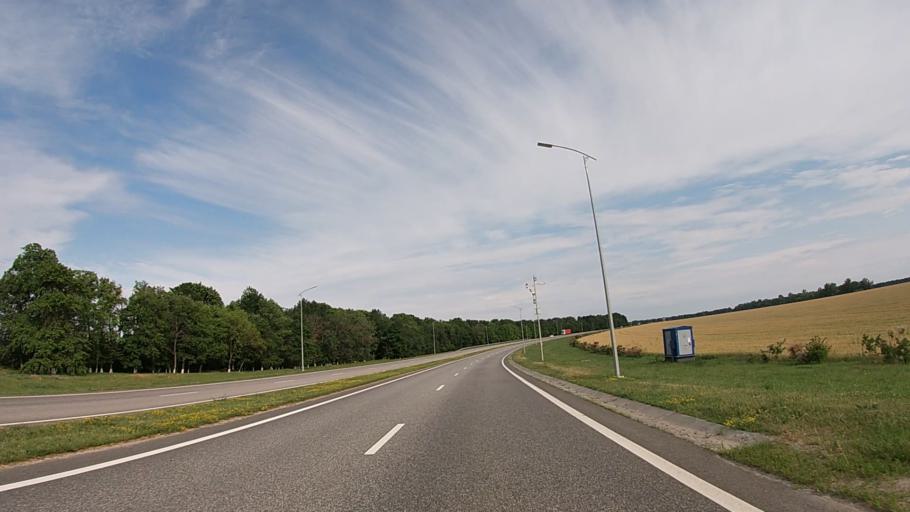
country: RU
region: Belgorod
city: Borisovka
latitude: 50.7540
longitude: 35.9681
